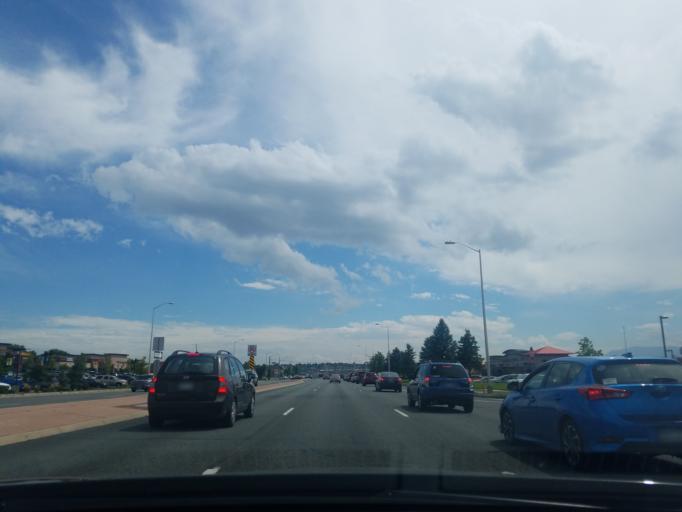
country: US
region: Colorado
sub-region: El Paso County
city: Air Force Academy
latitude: 38.9393
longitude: -104.7990
